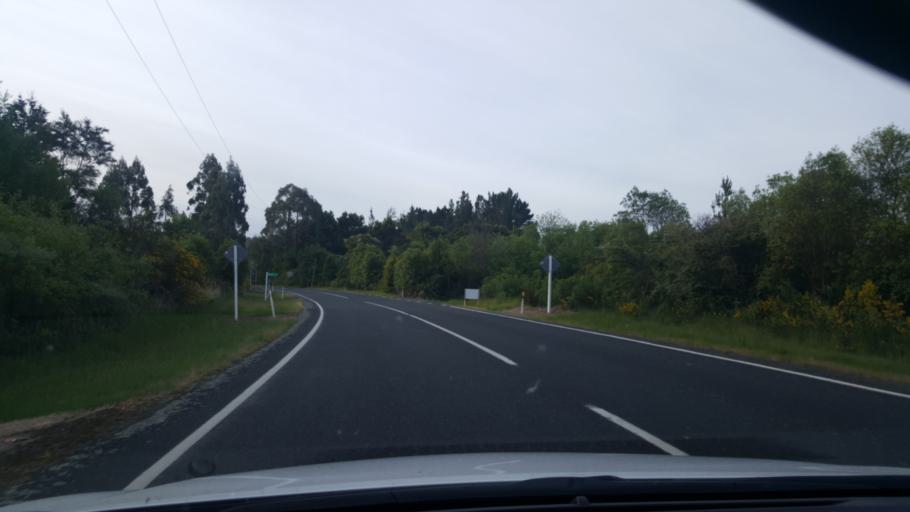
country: NZ
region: Waikato
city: Turangi
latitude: -38.9614
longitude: 175.7646
